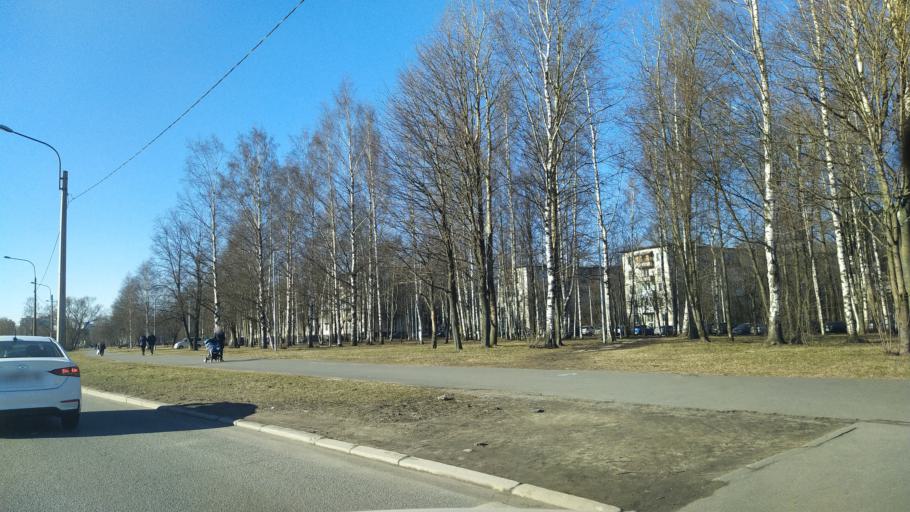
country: RU
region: Leningrad
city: Akademicheskoe
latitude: 59.9981
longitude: 30.4322
